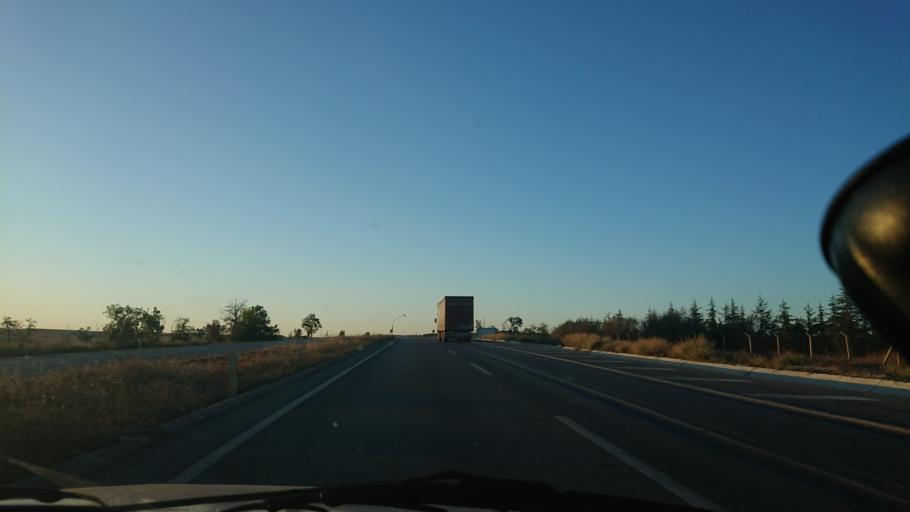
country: TR
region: Eskisehir
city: Mahmudiye
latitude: 39.4842
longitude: 30.9861
